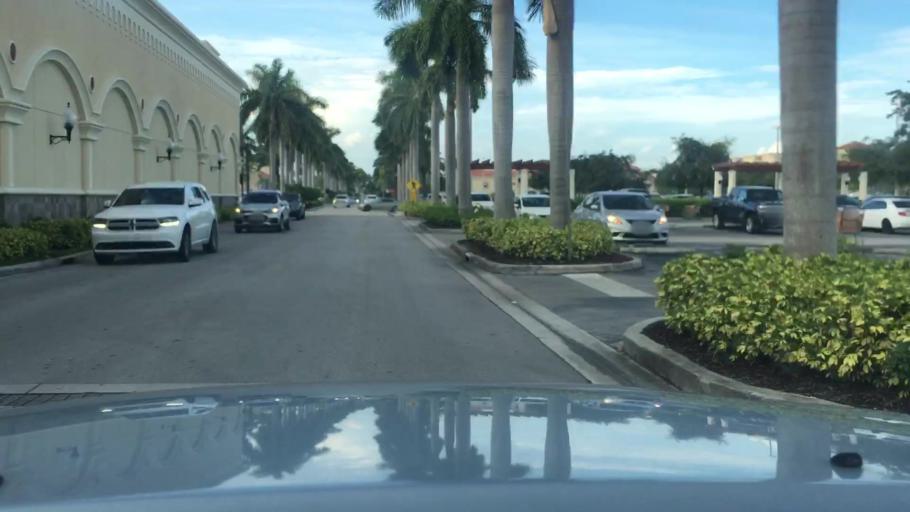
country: US
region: Florida
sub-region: Miami-Dade County
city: Three Lakes
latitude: 25.6528
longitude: -80.4135
